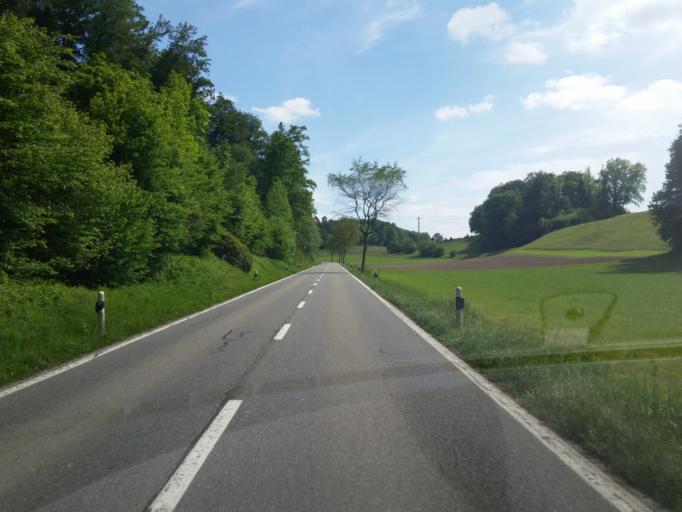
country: CH
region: Aargau
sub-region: Bezirk Bremgarten
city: Unterlunkhofen
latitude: 47.3146
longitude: 8.3543
